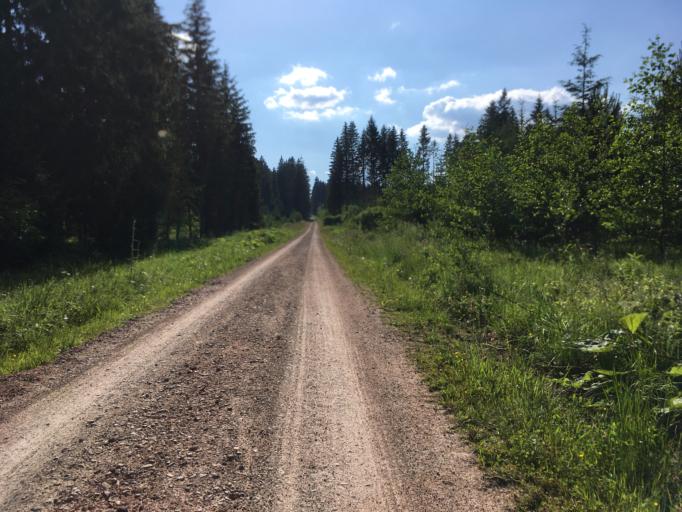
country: DE
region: Baden-Wuerttemberg
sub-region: Freiburg Region
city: Eisenbach
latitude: 47.9351
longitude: 8.3186
